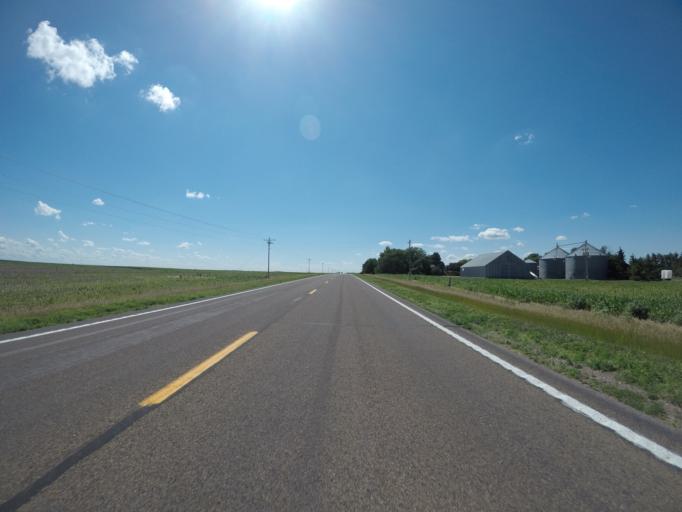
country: US
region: Nebraska
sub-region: Chase County
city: Imperial
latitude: 40.5376
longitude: -101.6751
